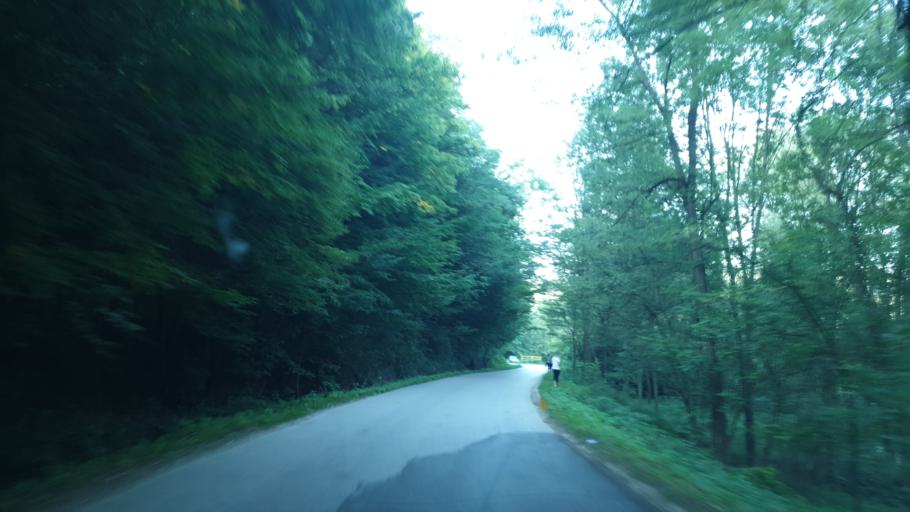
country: RS
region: Central Serbia
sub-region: Zlatiborski Okrug
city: Pozega
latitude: 43.8754
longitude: 19.9937
